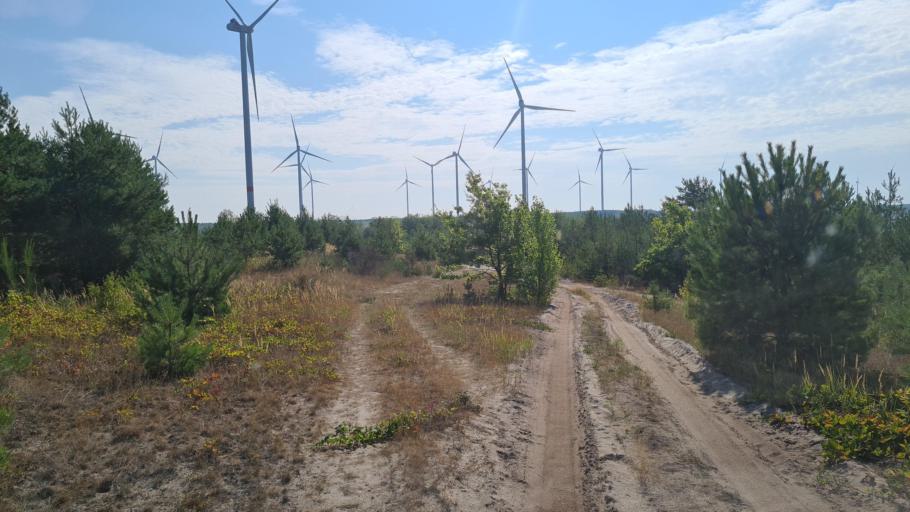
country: DE
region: Brandenburg
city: Sallgast
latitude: 51.5509
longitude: 13.8392
